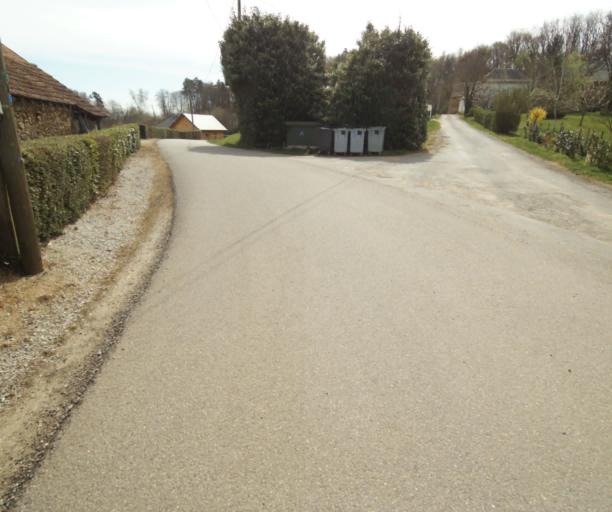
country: FR
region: Limousin
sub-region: Departement de la Correze
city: Naves
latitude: 45.3005
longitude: 1.7643
